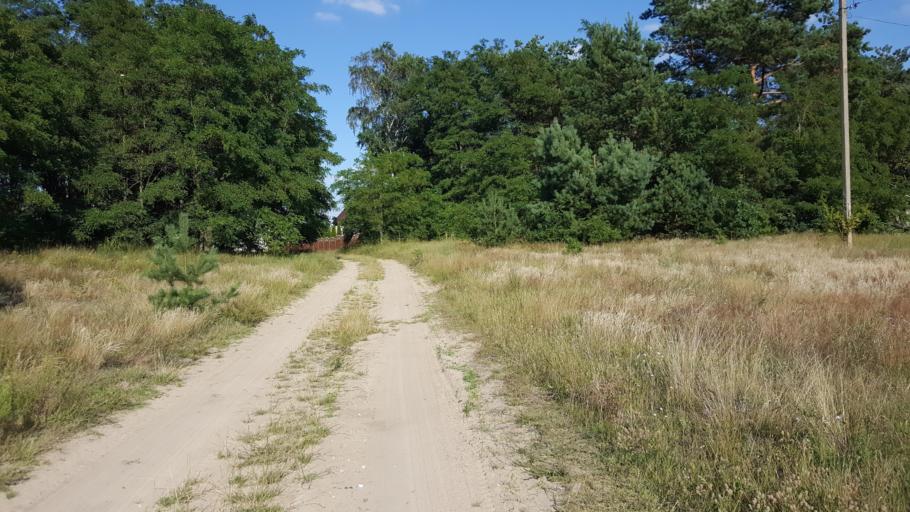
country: BY
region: Brest
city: Kamyanyets
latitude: 52.3840
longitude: 23.7469
